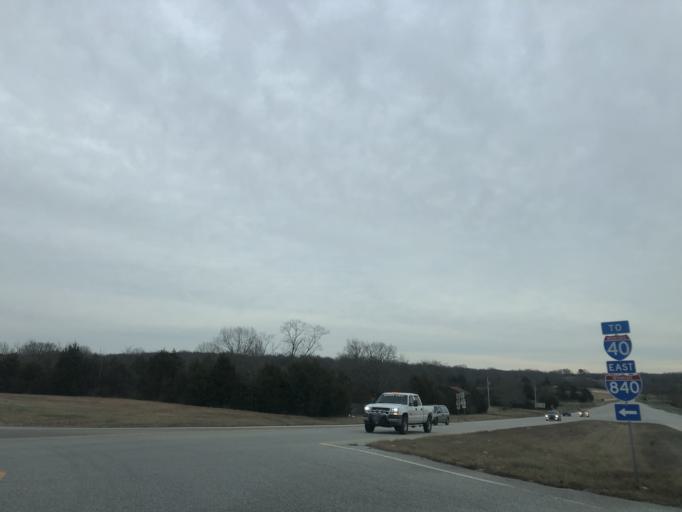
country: US
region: Tennessee
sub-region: Wilson County
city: Rural Hill
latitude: 36.1291
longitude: -86.3954
